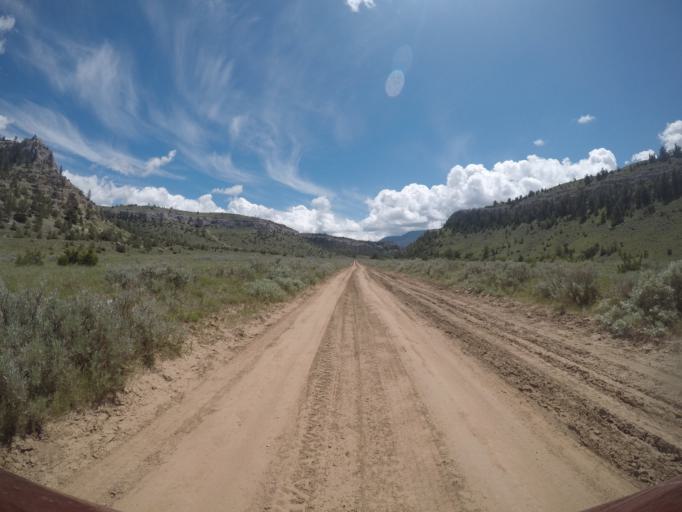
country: US
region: Wyoming
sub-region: Big Horn County
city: Lovell
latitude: 45.2316
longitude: -108.6101
